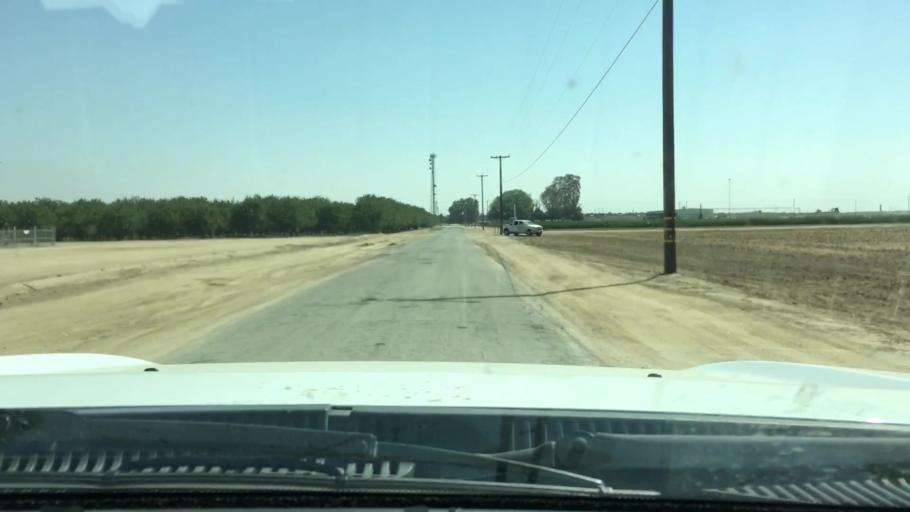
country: US
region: California
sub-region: Kern County
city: Shafter
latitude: 35.5364
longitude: -119.2747
